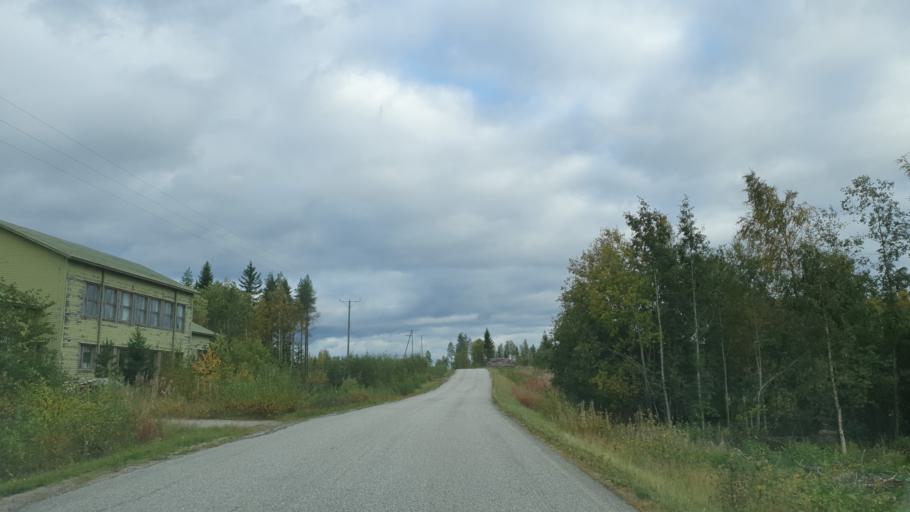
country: FI
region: Kainuu
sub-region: Kehys-Kainuu
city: Kuhmo
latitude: 63.9548
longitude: 29.7338
